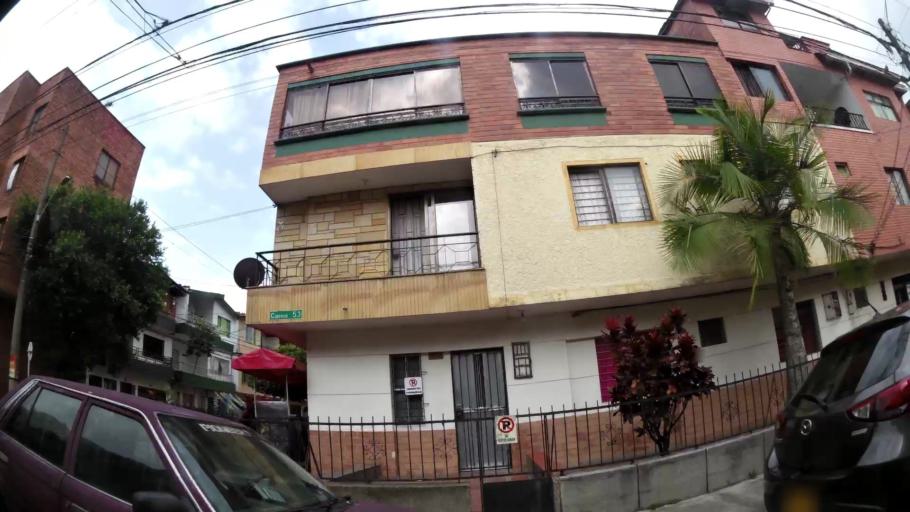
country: CO
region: Antioquia
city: Itagui
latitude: 6.2082
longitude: -75.5862
